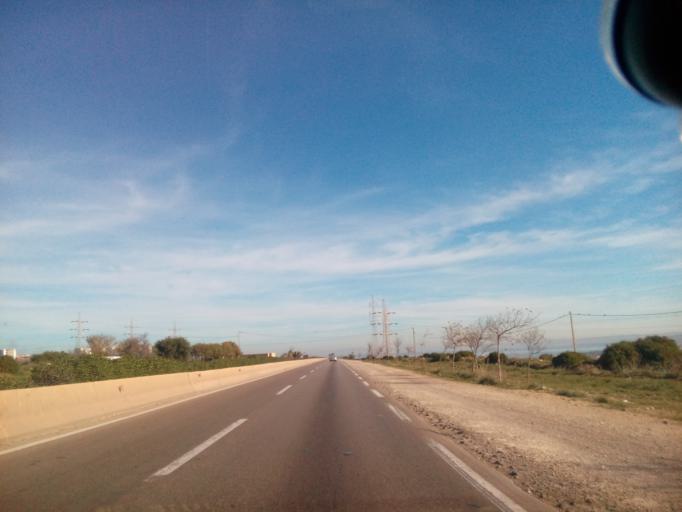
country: DZ
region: Oran
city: Ain el Bya
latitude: 35.7801
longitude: -0.1871
